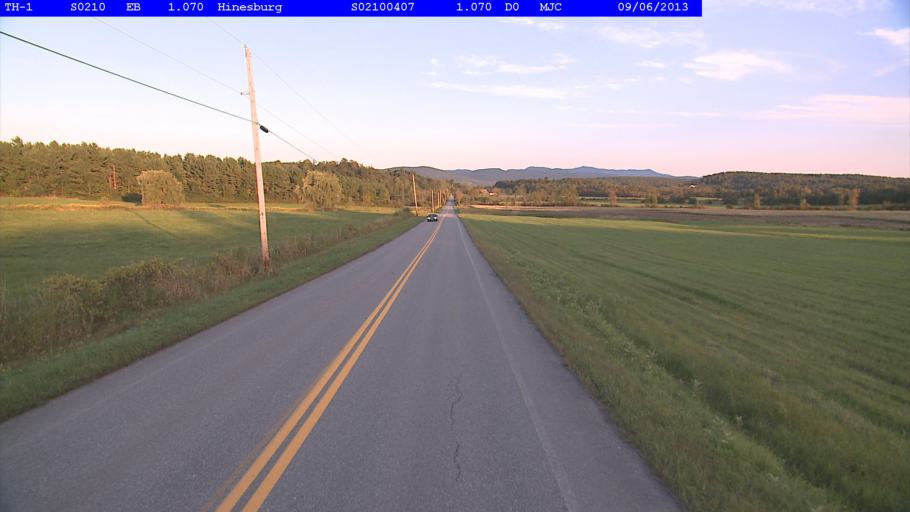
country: US
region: Vermont
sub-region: Chittenden County
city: Hinesburg
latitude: 44.3499
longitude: -73.1499
